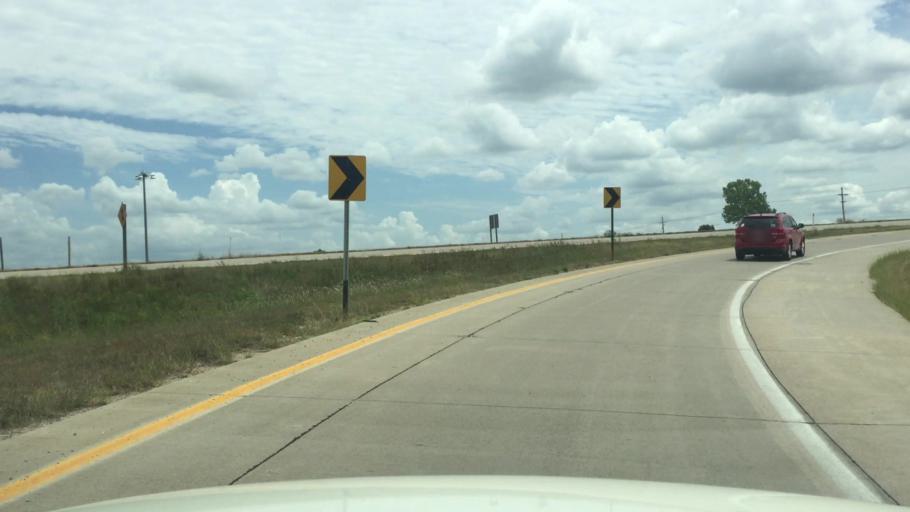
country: US
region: Kansas
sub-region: Shawnee County
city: Topeka
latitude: 39.0464
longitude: -95.6026
